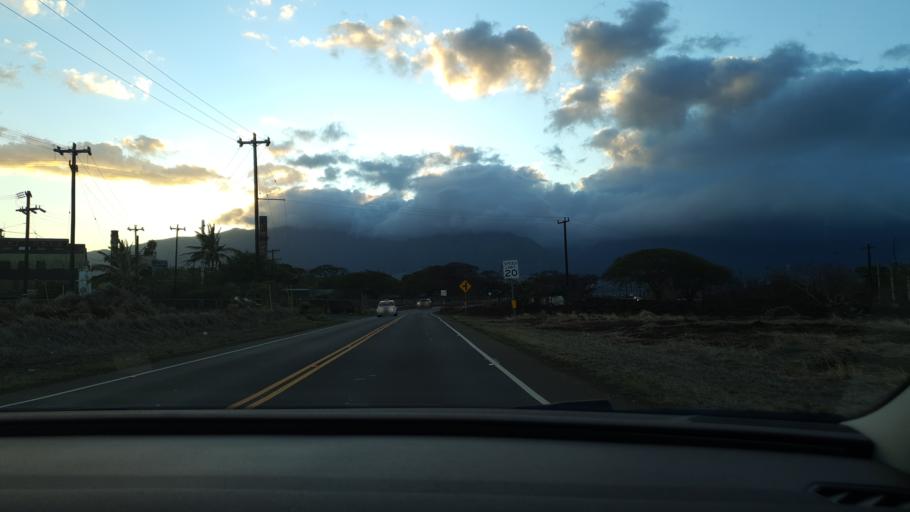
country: US
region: Hawaii
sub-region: Maui County
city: Kahului
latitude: 20.8692
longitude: -156.4503
